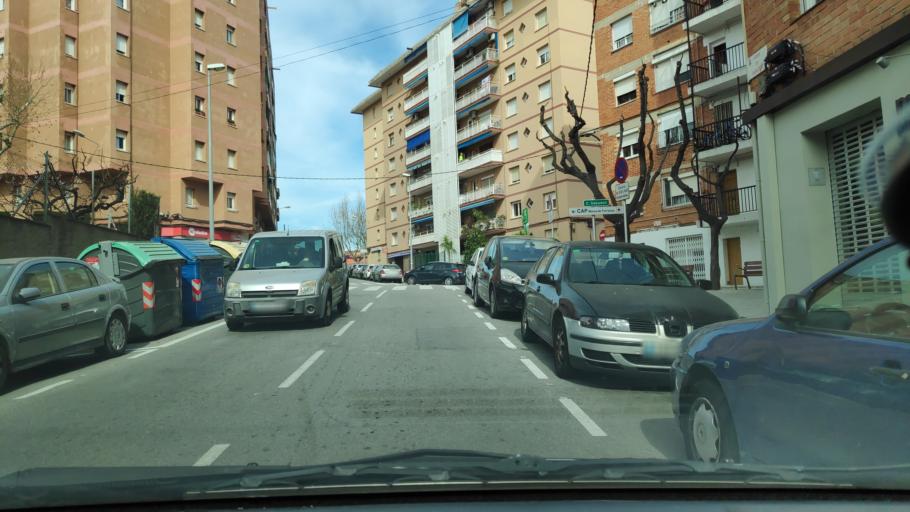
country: ES
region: Catalonia
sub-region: Provincia de Barcelona
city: Rubi
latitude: 41.4953
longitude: 2.0343
